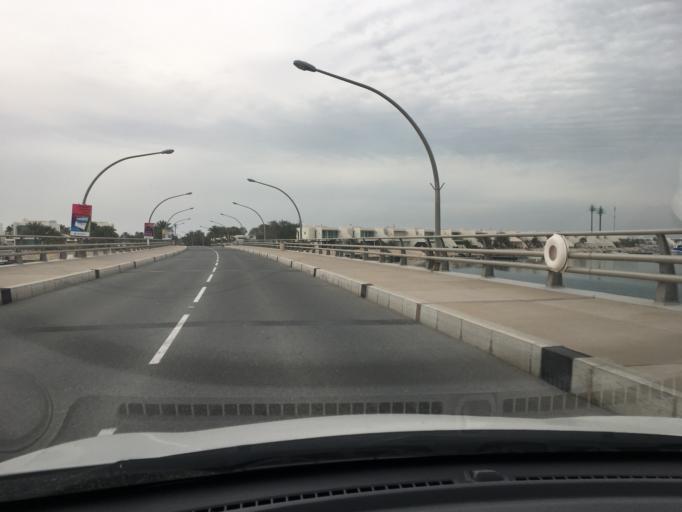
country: BH
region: Central Governorate
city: Dar Kulayb
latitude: 25.8362
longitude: 50.6150
